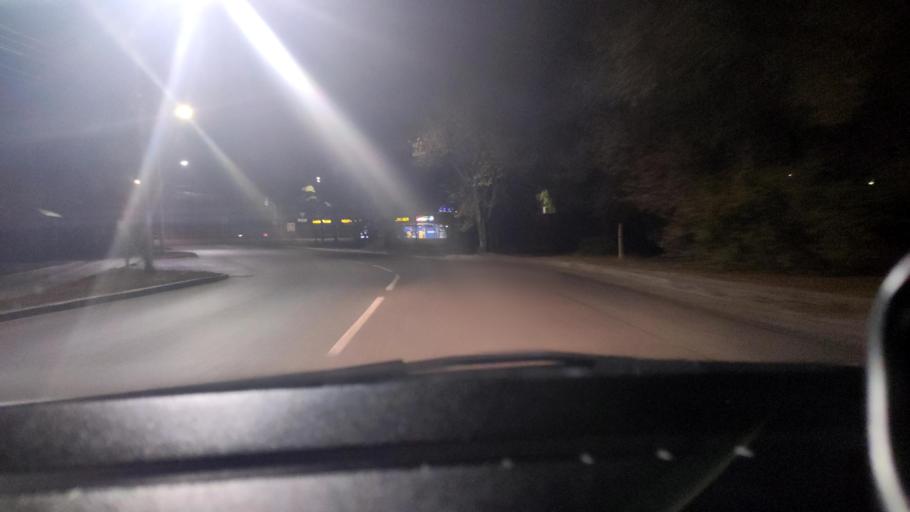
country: RU
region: Voronezj
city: Pridonskoy
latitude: 51.6493
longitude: 39.1002
